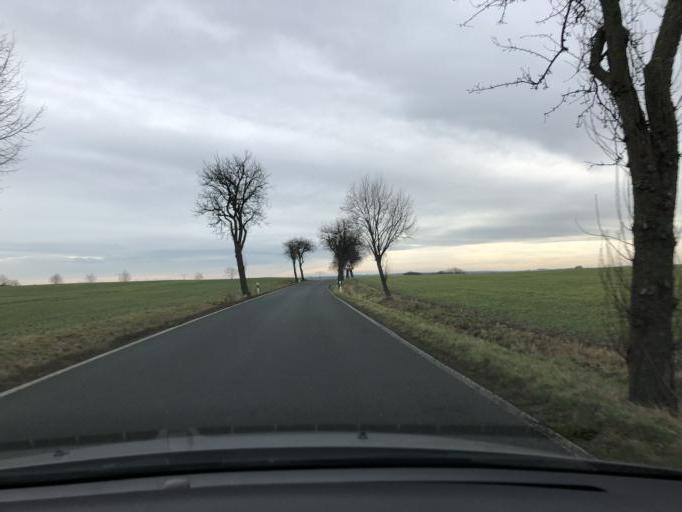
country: DE
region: Saxony
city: Nossen
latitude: 51.0702
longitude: 13.3074
